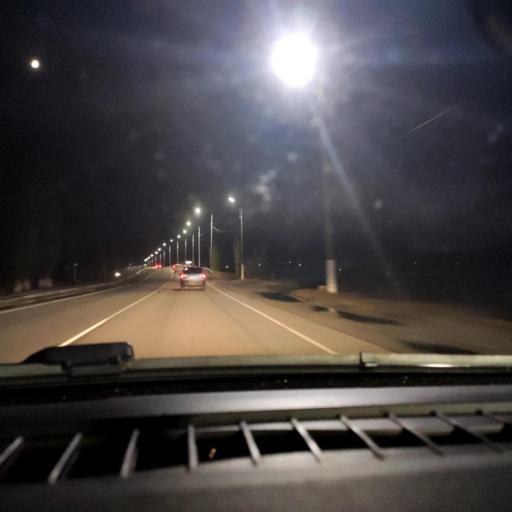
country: RU
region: Voronezj
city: Novaya Usman'
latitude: 51.6276
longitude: 39.4000
